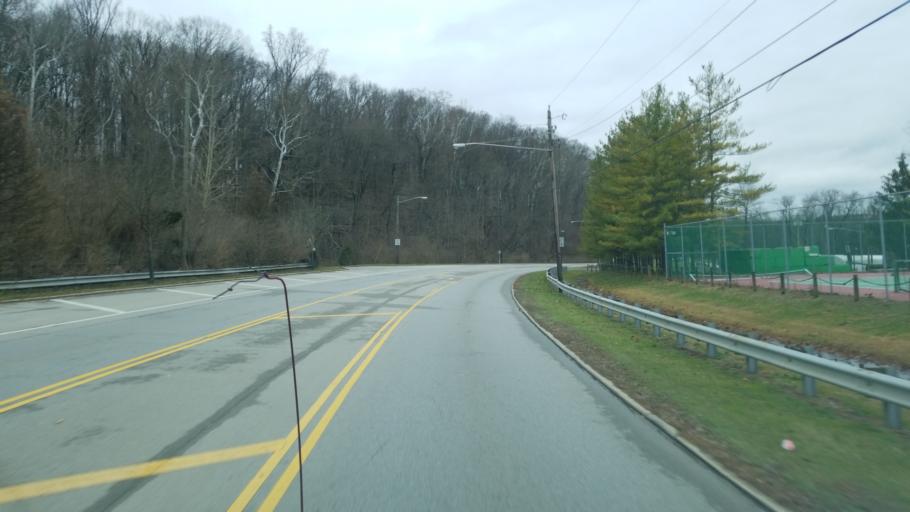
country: US
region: Kentucky
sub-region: Campbell County
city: Fort Thomas
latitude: 39.0822
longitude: -84.4200
